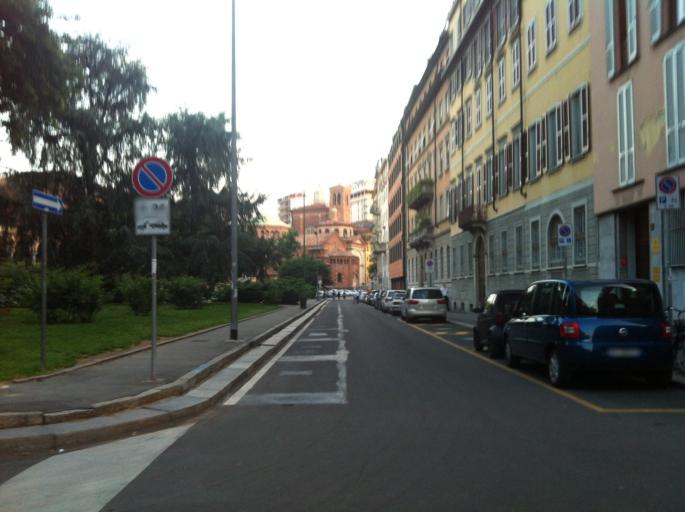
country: IT
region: Lombardy
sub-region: Citta metropolitana di Milano
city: Milano
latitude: 45.4605
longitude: 9.1931
